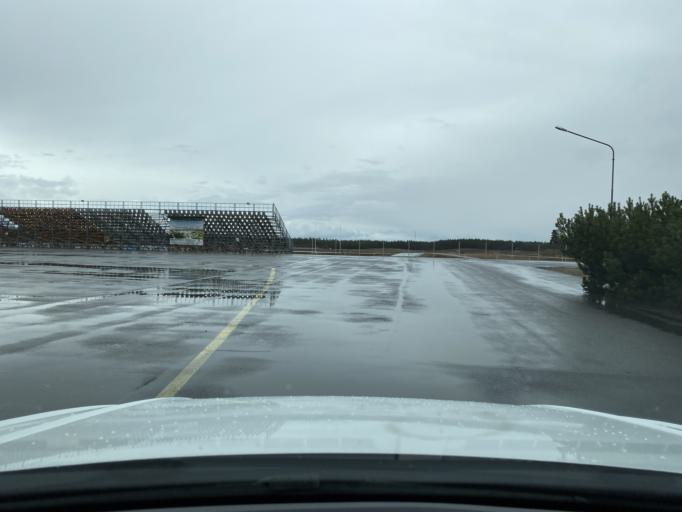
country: FI
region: Satakunta
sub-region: Pori
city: Vampula
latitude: 60.9747
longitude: 22.6566
